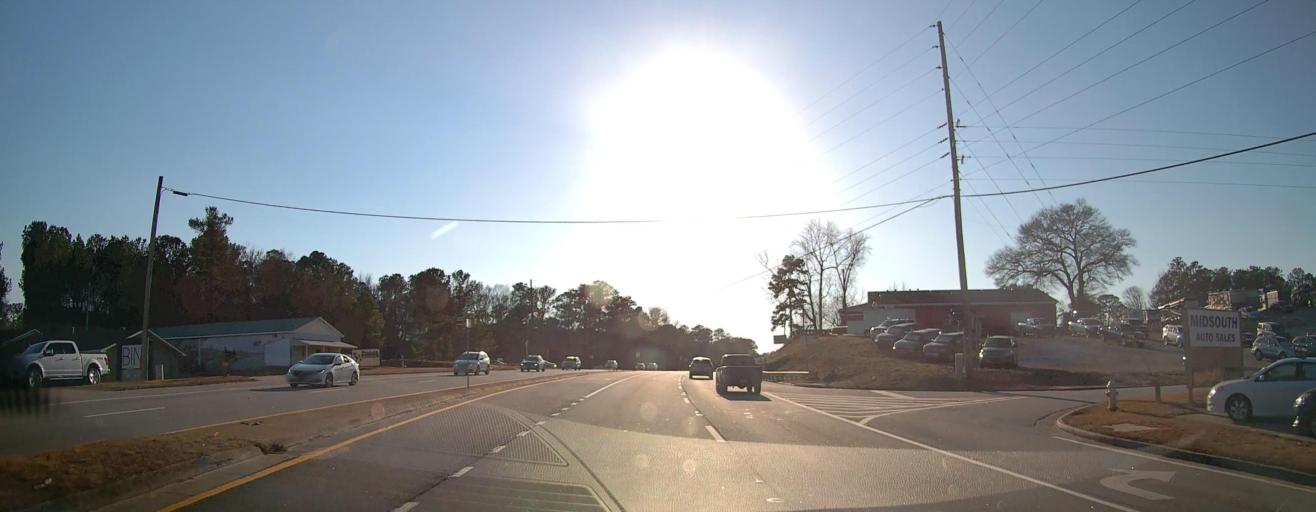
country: US
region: Georgia
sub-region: Fayette County
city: Fayetteville
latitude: 33.4547
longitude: -84.4242
